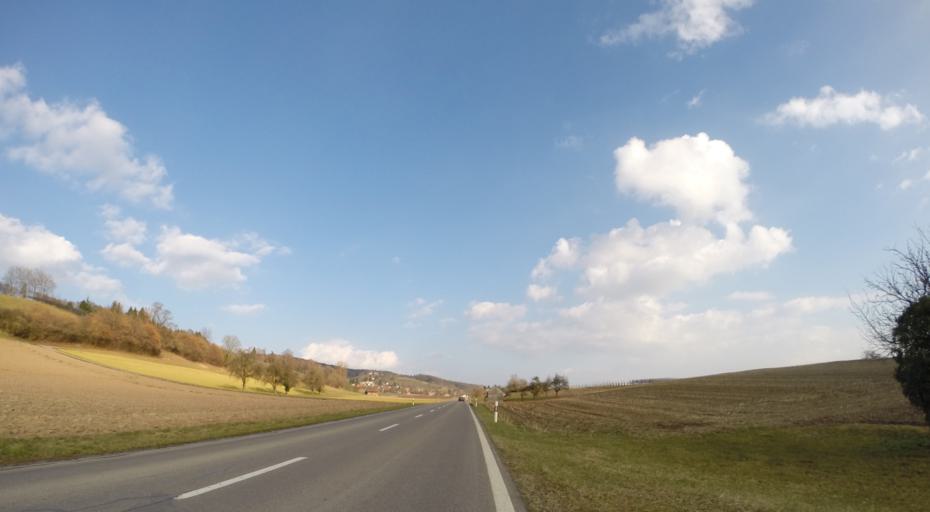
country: CH
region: Thurgau
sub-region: Frauenfeld District
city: Wagenhausen
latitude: 47.6269
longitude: 8.8153
